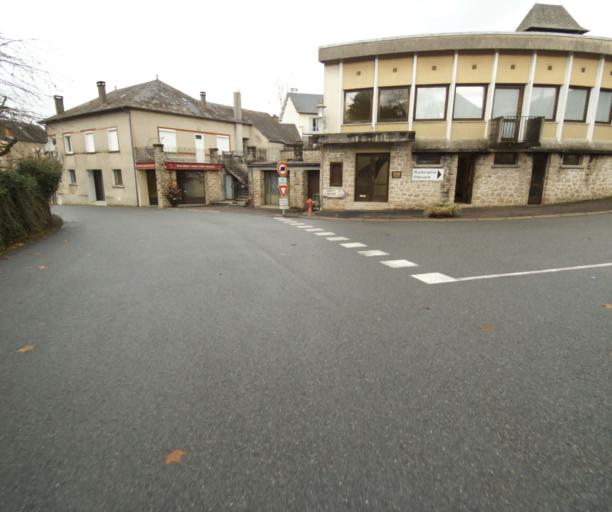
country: FR
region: Limousin
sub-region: Departement de la Correze
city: Saint-Mexant
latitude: 45.2733
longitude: 1.6348
